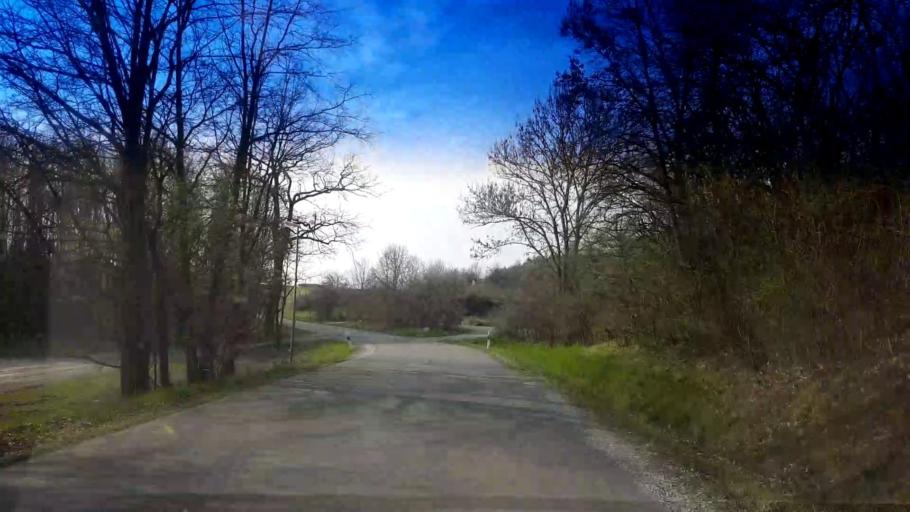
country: DE
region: Bavaria
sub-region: Upper Franconia
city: Neudrossenfeld
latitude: 50.0524
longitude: 11.4948
